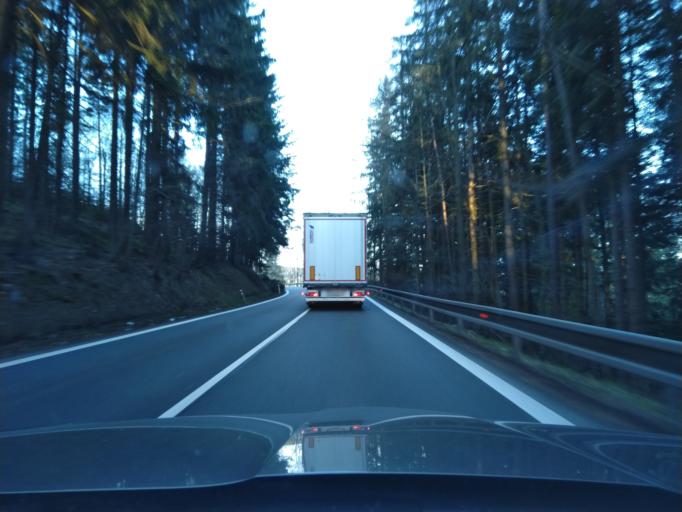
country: CZ
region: Jihocesky
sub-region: Okres Prachatice
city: Vimperk
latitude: 49.0369
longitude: 13.7628
